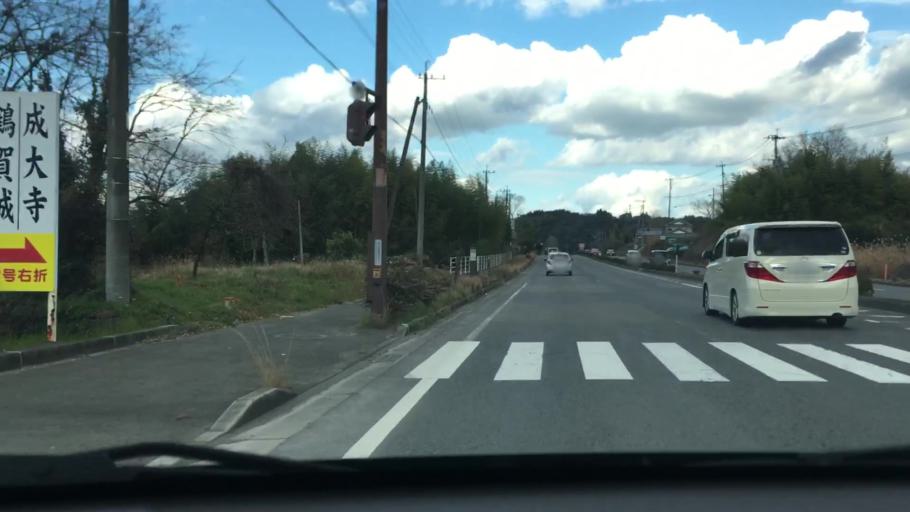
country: JP
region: Oita
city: Oita
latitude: 33.1271
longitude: 131.6564
